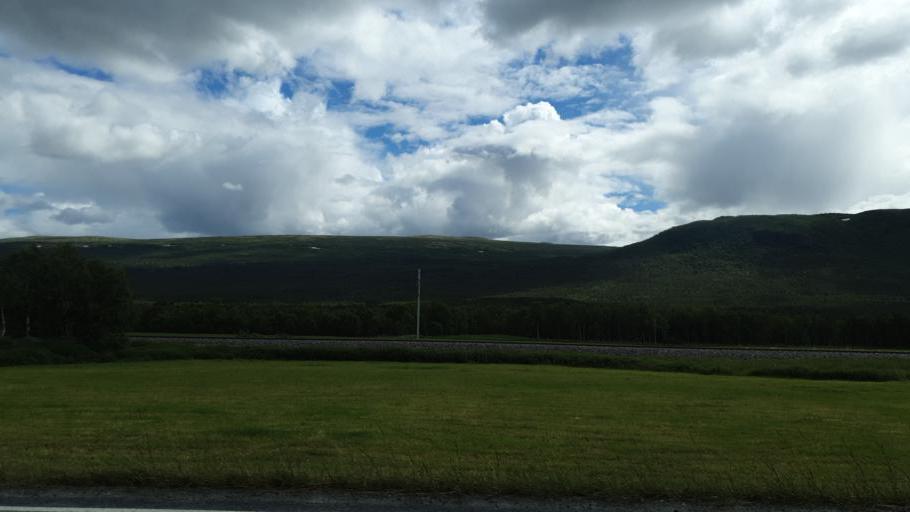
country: NO
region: Sor-Trondelag
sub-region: Oppdal
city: Oppdal
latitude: 62.6011
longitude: 9.7225
